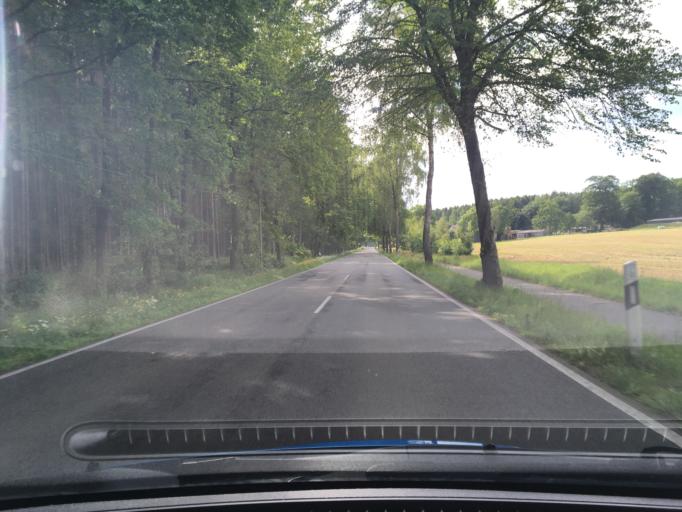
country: DE
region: Lower Saxony
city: Welle
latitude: 53.2498
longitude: 9.7740
